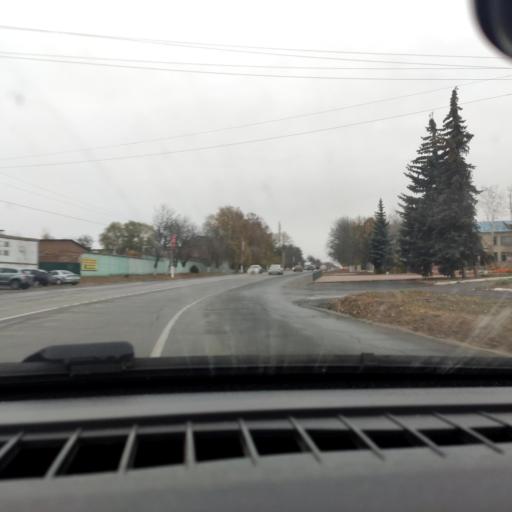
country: RU
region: Voronezj
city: Ostrogozhsk
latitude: 50.8710
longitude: 39.0736
